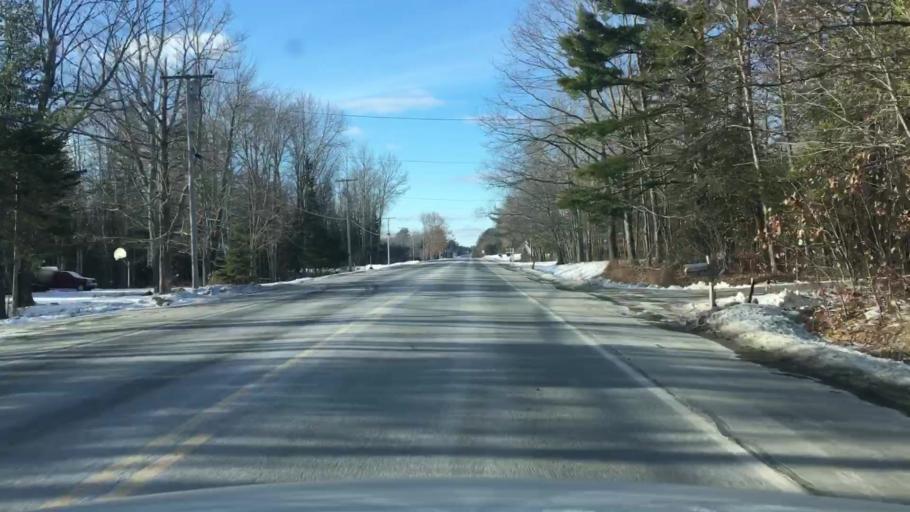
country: US
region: Maine
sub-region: Penobscot County
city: Holden
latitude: 44.8034
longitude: -68.6021
